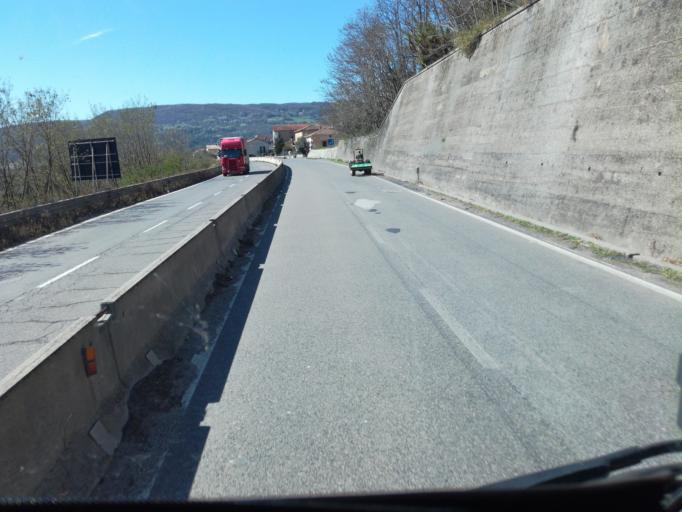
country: IT
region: Latium
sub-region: Provincia di Viterbo
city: Orte Scalo
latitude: 42.4573
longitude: 12.4134
